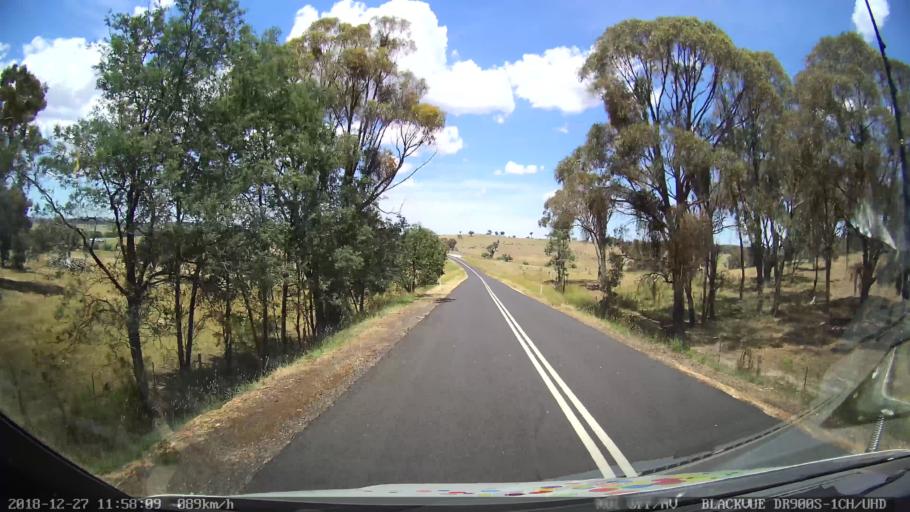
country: AU
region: New South Wales
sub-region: Blayney
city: Blayney
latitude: -33.7203
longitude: 149.3860
